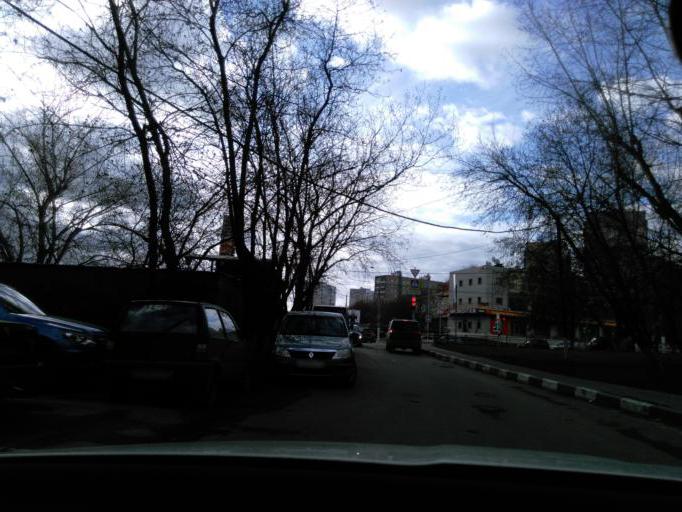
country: RU
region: Moscow
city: Novyye Cheremushki
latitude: 55.6909
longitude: 37.5979
